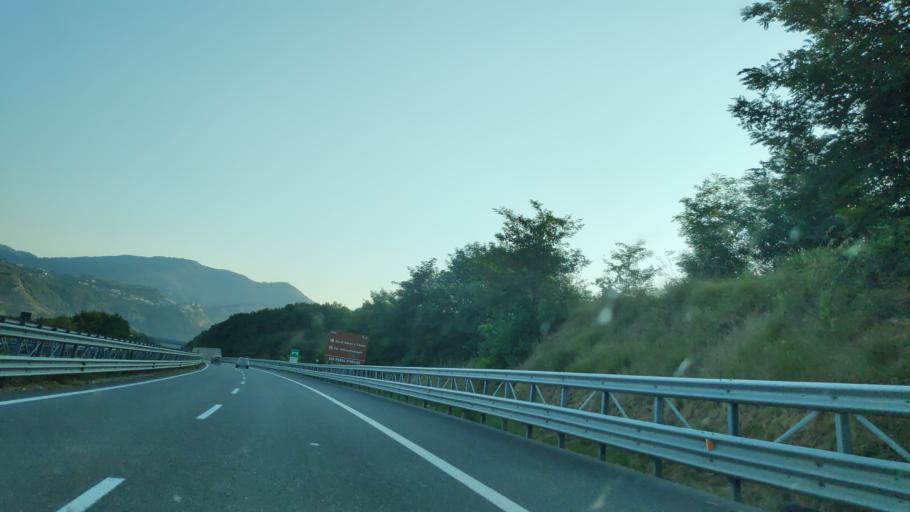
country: IT
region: Calabria
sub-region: Provincia di Catanzaro
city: Nocera Terinese
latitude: 39.0502
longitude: 16.1513
